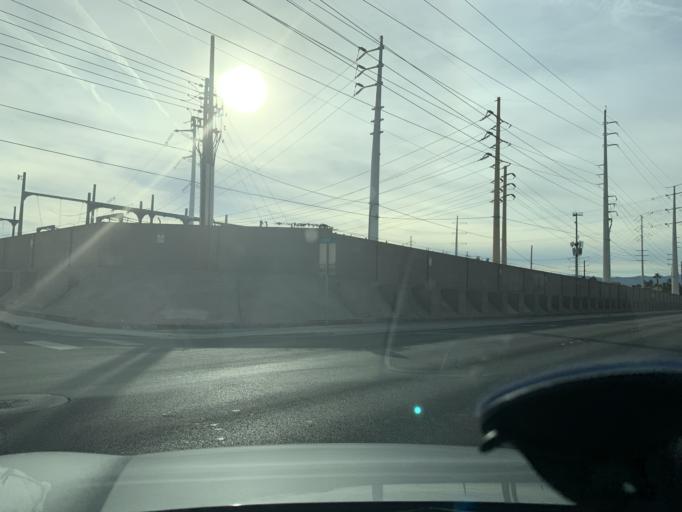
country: US
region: Nevada
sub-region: Clark County
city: Spring Valley
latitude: 36.1152
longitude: -115.2123
